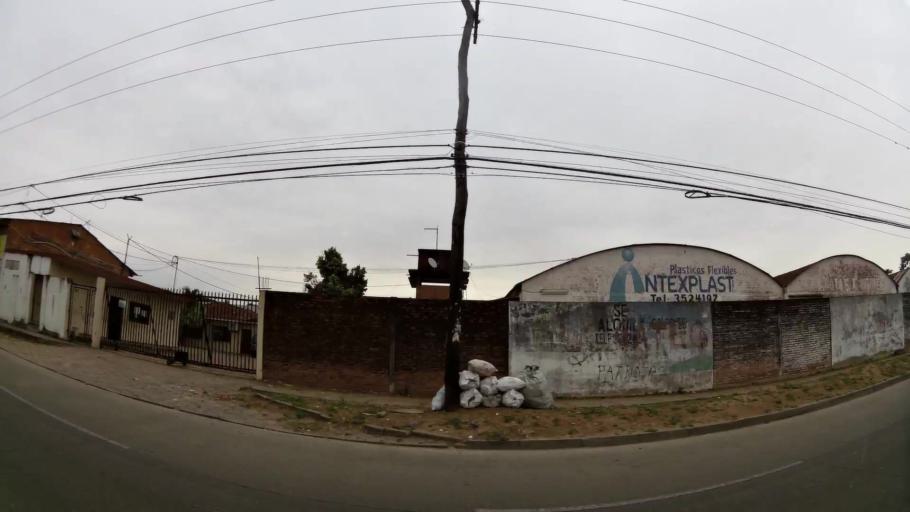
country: BO
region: Santa Cruz
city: Santa Cruz de la Sierra
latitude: -17.8112
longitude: -63.1818
